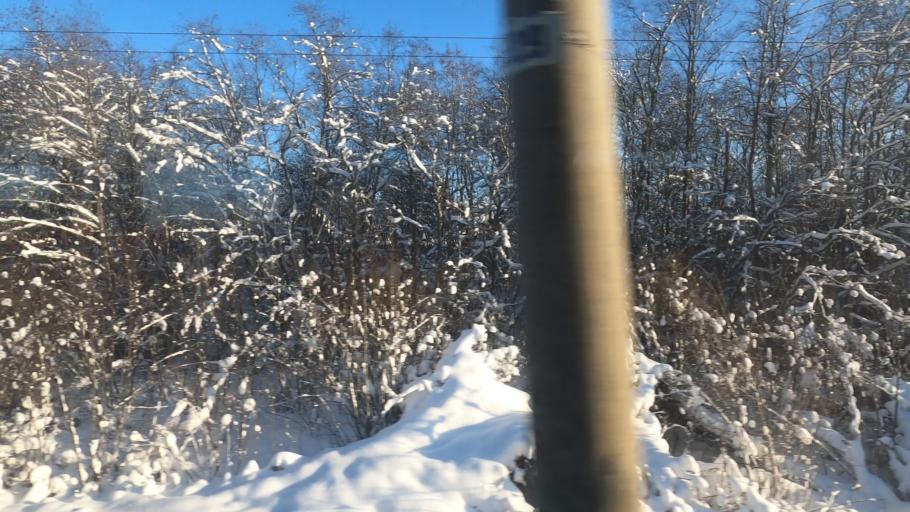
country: RU
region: Moskovskaya
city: Novo-Nikol'skoye
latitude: 56.5617
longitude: 37.5660
